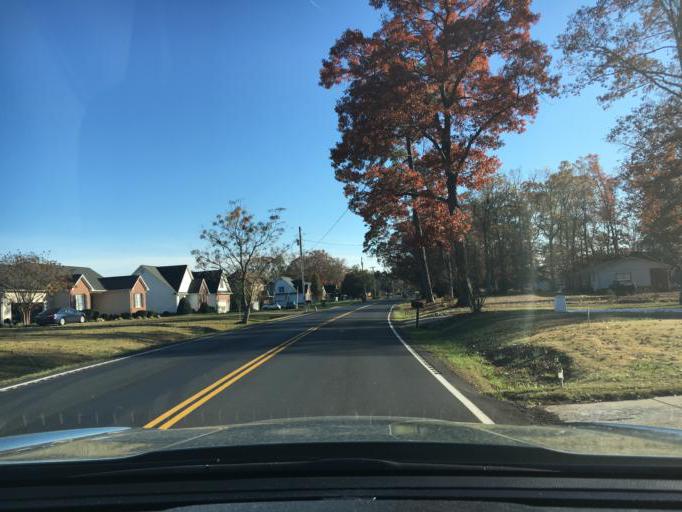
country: US
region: South Carolina
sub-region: Spartanburg County
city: Inman
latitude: 35.0121
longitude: -82.0755
